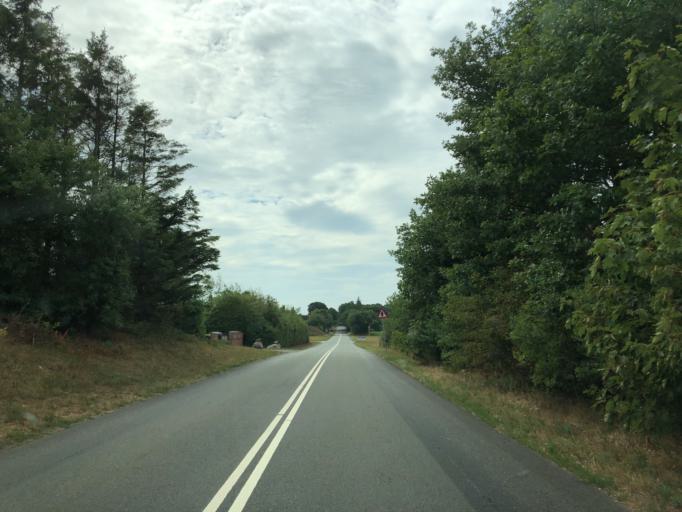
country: DK
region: South Denmark
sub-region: Vejle Kommune
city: Egtved
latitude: 55.6185
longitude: 9.1920
